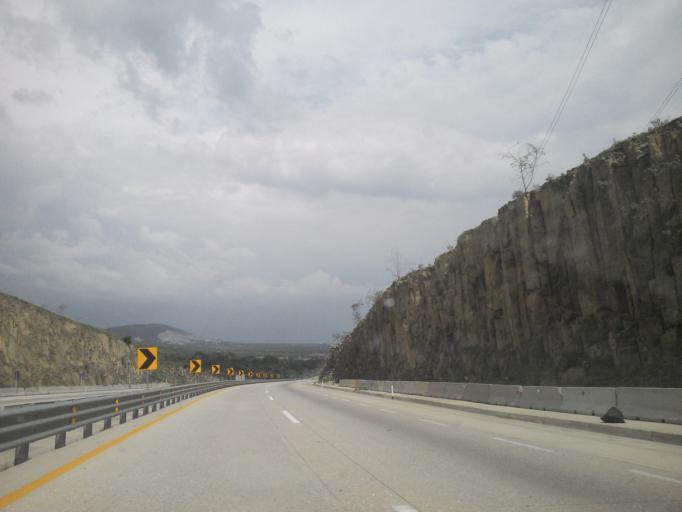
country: MX
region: Mexico
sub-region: Apaxco
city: Colonia Juarez
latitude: 20.0147
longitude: -99.1541
